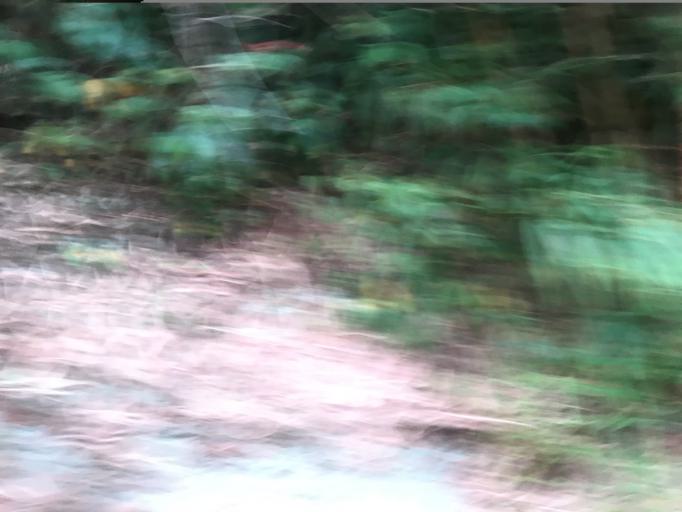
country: CO
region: Valle del Cauca
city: Cali
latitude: 3.4830
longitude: -76.6089
